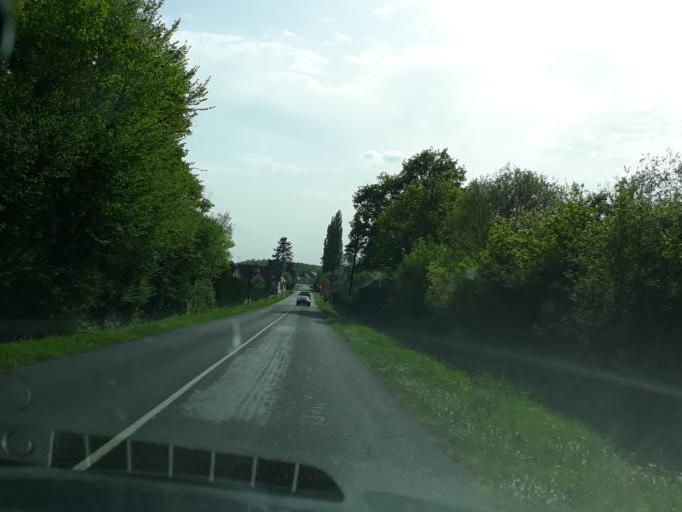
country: FR
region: Centre
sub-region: Departement du Loir-et-Cher
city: Saint-Laurent-Nouan
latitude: 47.6540
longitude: 1.6142
